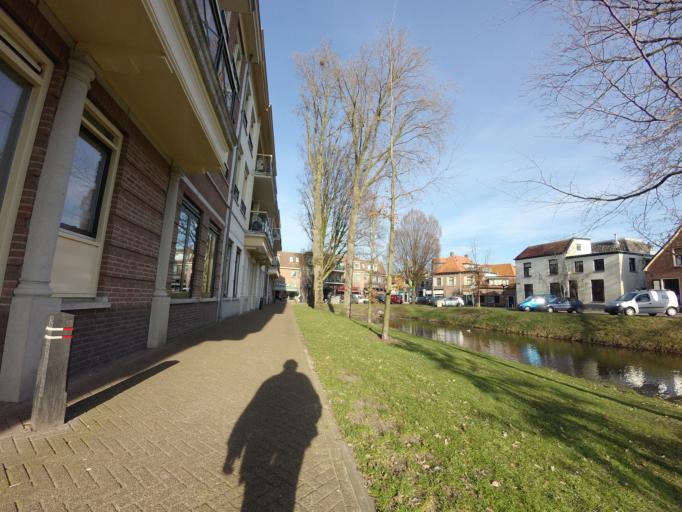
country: NL
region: Gelderland
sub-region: Gemeente Lochem
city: Lochem
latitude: 52.1620
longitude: 6.4118
